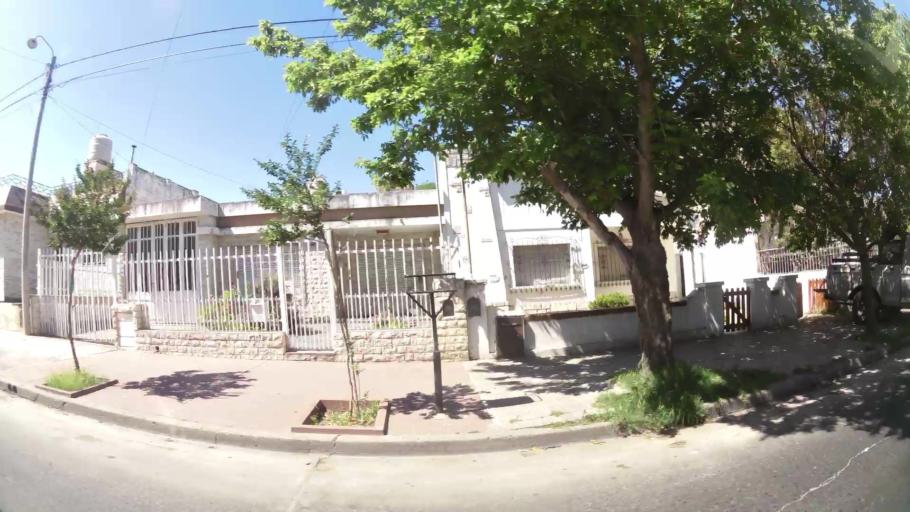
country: AR
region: Cordoba
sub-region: Departamento de Capital
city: Cordoba
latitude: -31.4230
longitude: -64.1401
